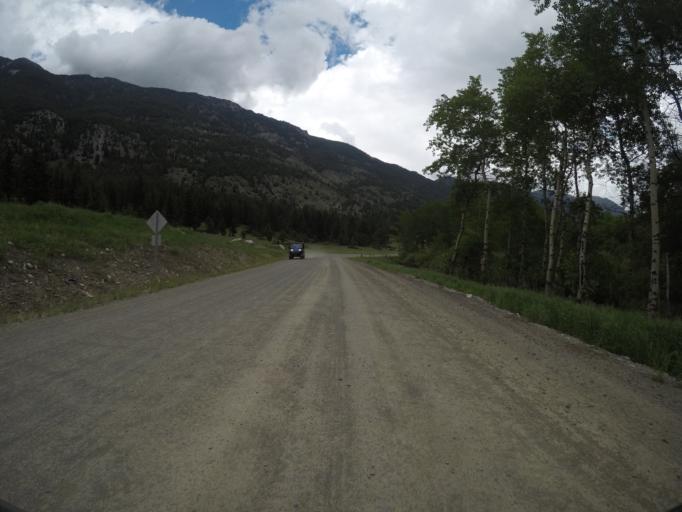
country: US
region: Montana
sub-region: Park County
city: Livingston
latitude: 45.4864
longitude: -110.2148
